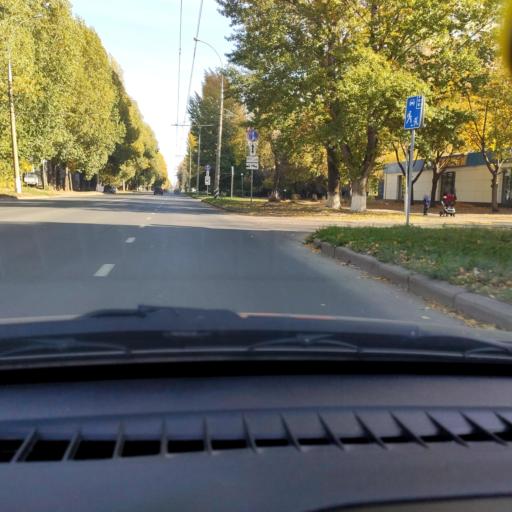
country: RU
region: Samara
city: Tol'yatti
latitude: 53.5387
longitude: 49.2697
